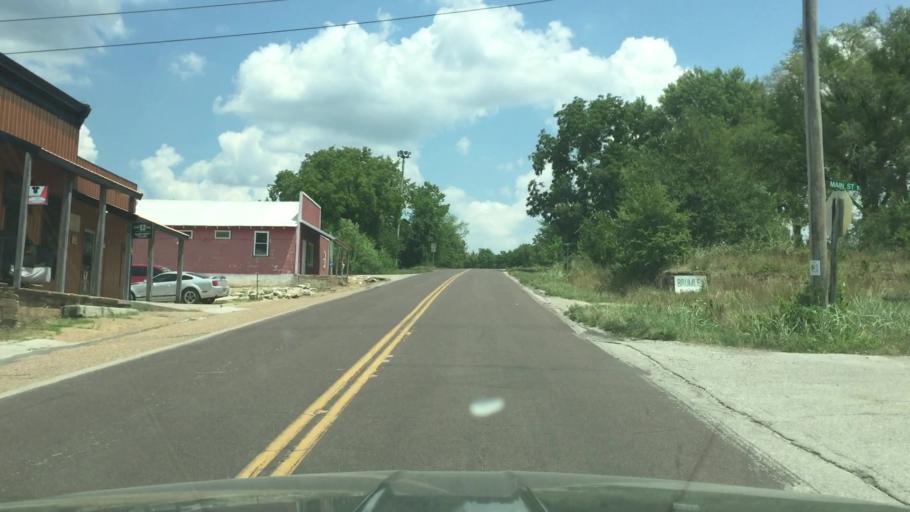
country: US
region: Missouri
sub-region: Miller County
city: Tuscumbia
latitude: 38.0864
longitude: -92.4875
